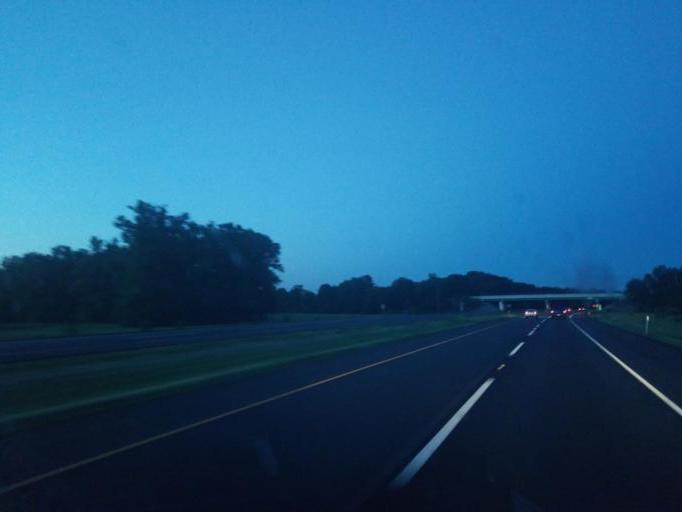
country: US
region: Indiana
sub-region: Saint Joseph County
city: Granger
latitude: 41.7321
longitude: -86.0455
